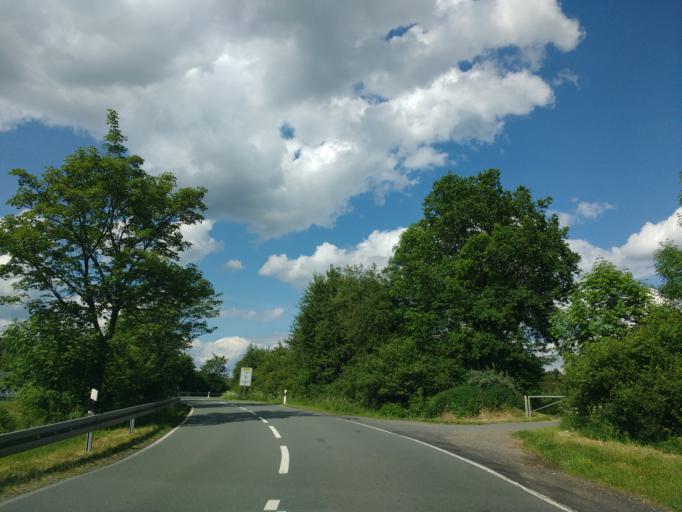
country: DE
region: Hesse
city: Battenberg
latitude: 50.9920
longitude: 8.6216
